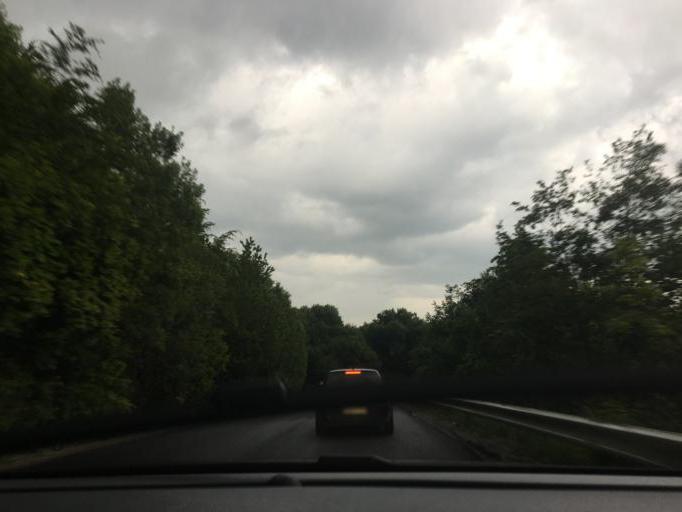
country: MK
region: Gostivar
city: Vrutok
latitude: 41.6775
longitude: 20.8490
